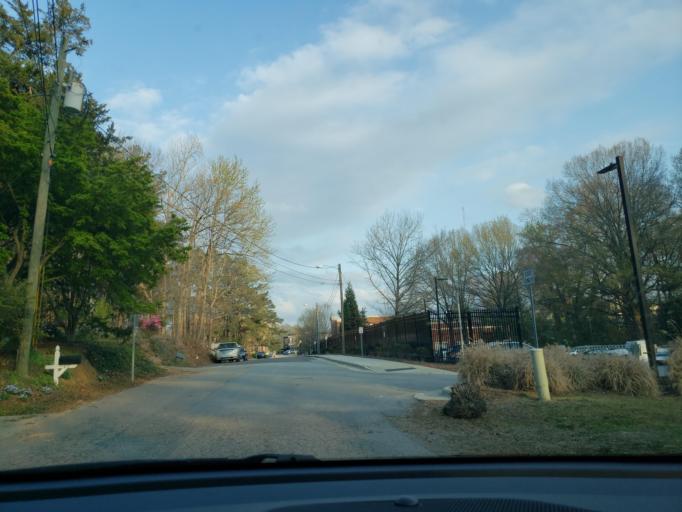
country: US
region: North Carolina
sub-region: Wake County
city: Apex
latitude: 35.7328
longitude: -78.8536
